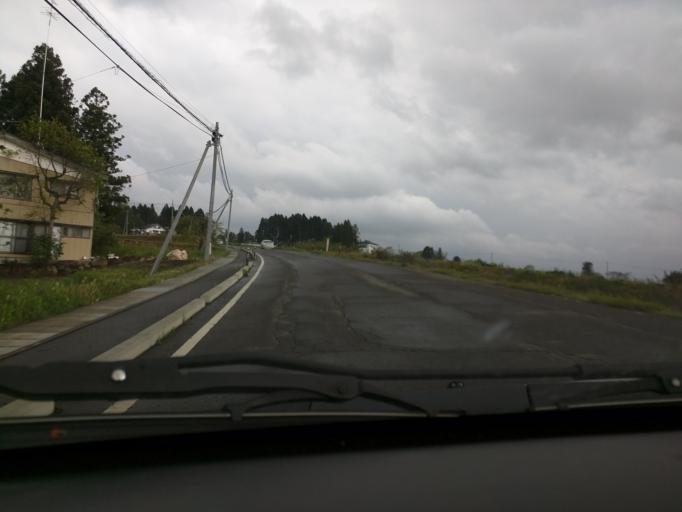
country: JP
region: Fukushima
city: Kitakata
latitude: 37.6335
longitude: 139.9344
